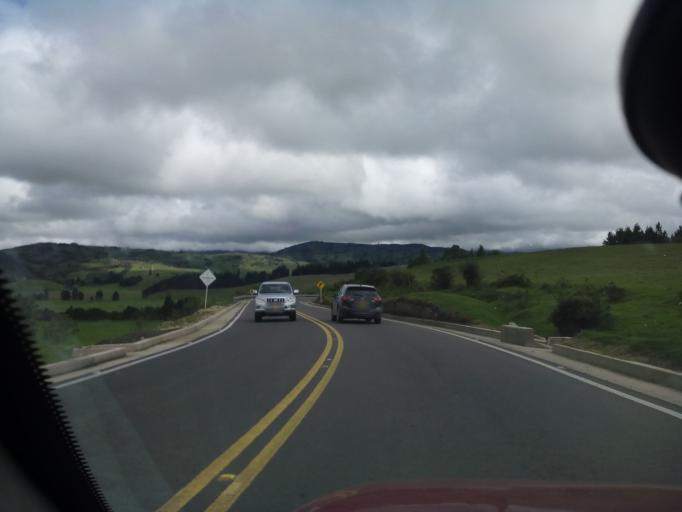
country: CO
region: Boyaca
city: Combita
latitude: 5.6385
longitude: -73.3500
